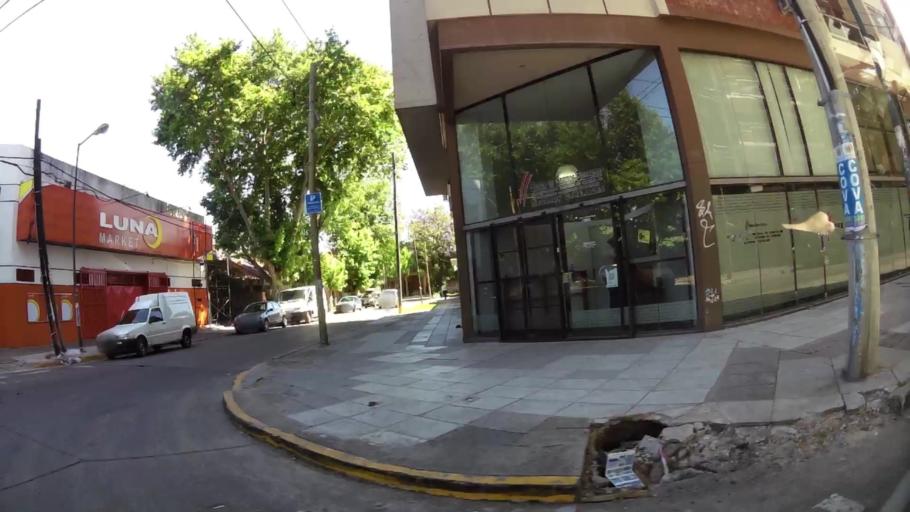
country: AR
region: Buenos Aires
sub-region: Partido de General San Martin
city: General San Martin
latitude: -34.5548
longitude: -58.5577
